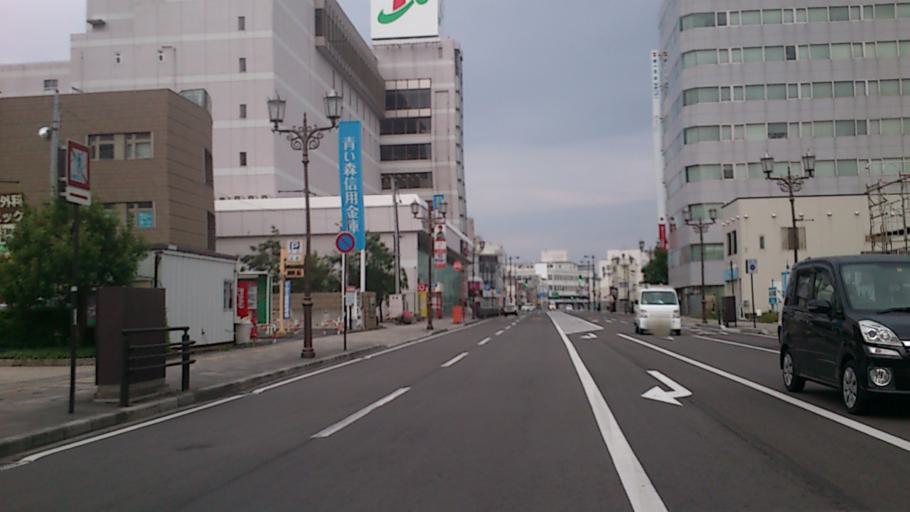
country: JP
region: Aomori
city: Hirosaki
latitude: 40.6001
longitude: 140.4825
